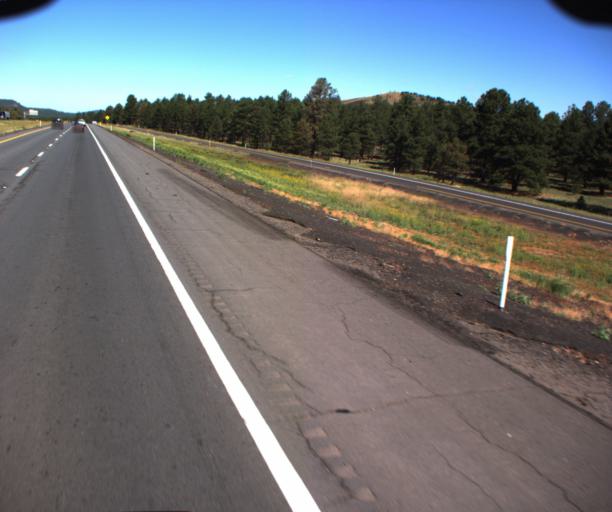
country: US
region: Arizona
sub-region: Coconino County
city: Williams
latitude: 35.2609
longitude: -112.1517
